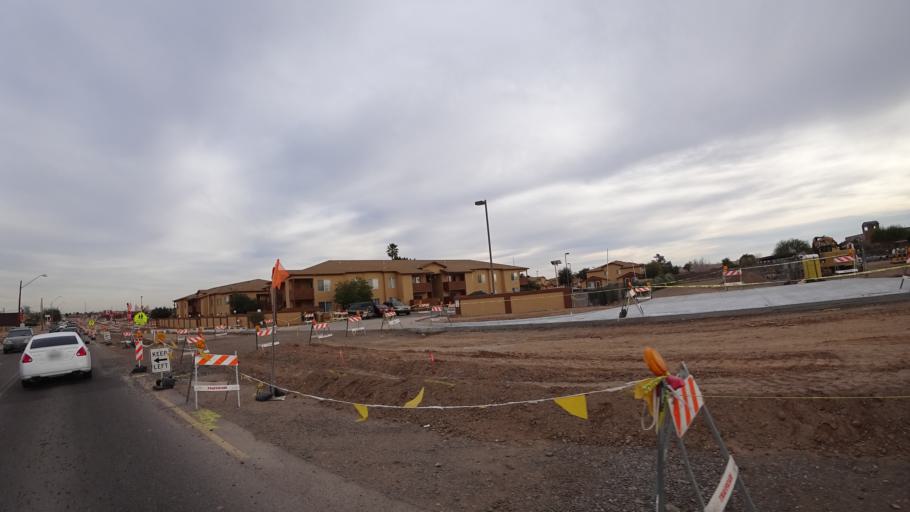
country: US
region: Arizona
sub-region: Maricopa County
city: El Mirage
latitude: 33.6090
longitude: -112.3235
